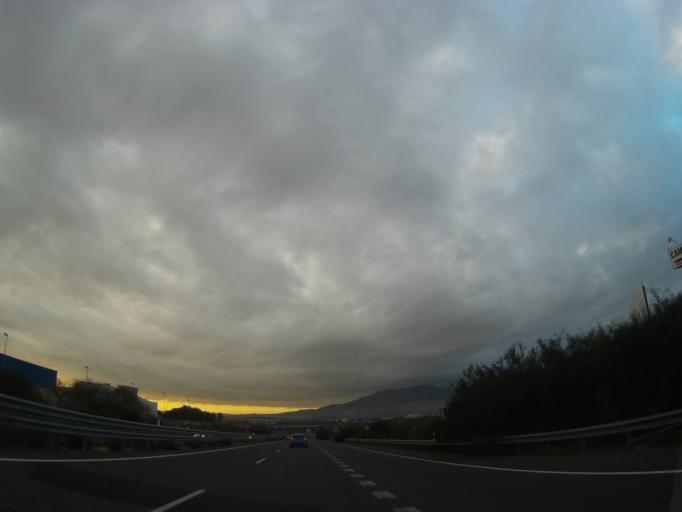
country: ES
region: Andalusia
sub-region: Provincia de Malaga
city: Alhaurin de la Torre
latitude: 36.7152
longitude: -4.5144
